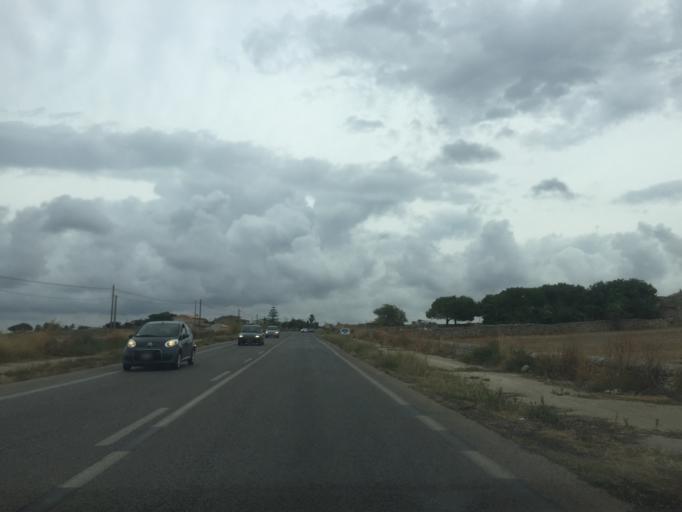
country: IT
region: Sicily
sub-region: Ragusa
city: Marina di Ragusa
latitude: 36.8085
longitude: 14.5647
